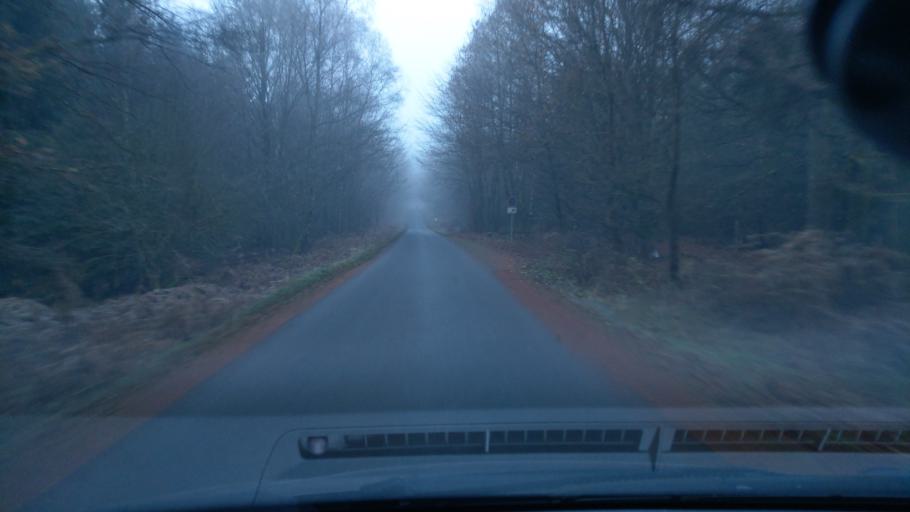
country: DE
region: Saarland
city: Tholey
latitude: 49.5081
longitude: 7.0140
